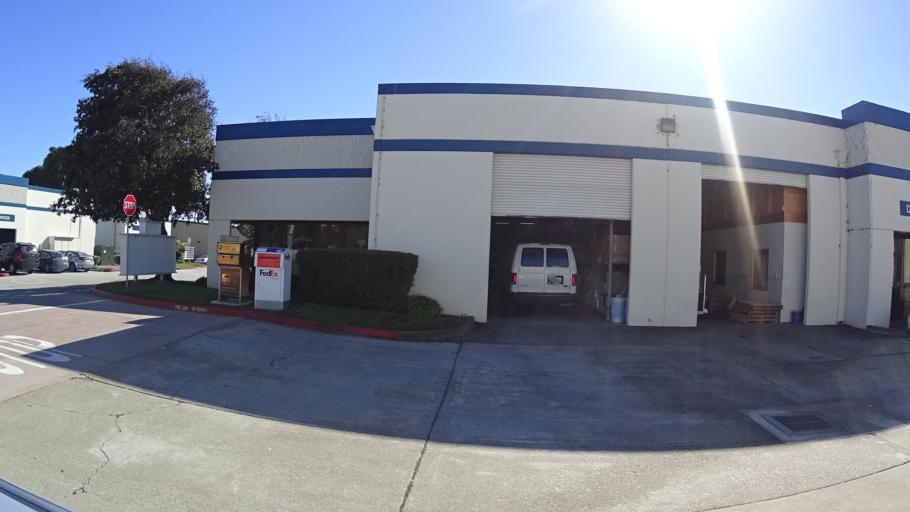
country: US
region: California
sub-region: San Mateo County
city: South San Francisco
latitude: 37.6524
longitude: -122.4150
